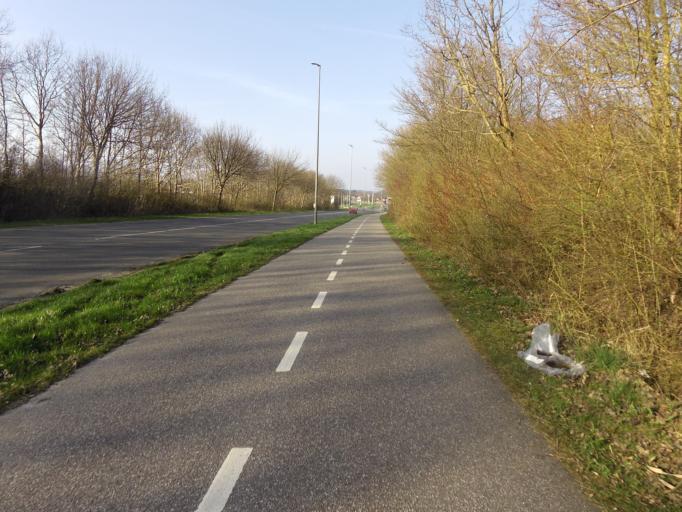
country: DK
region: South Denmark
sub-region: Vejen Kommune
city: Vejen
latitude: 55.4865
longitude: 9.1271
